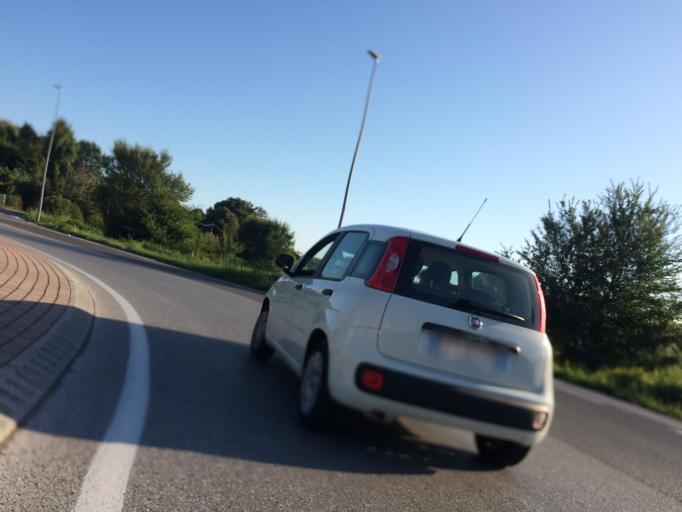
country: IT
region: Tuscany
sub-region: Provincia di Lucca
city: Camaiore
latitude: 43.8926
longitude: 10.2482
